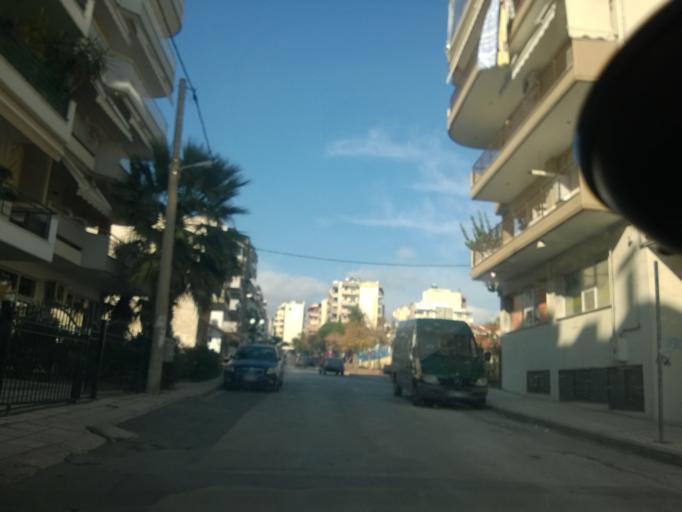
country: GR
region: Central Macedonia
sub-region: Nomos Thessalonikis
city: Stavroupoli
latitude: 40.6683
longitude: 22.9246
